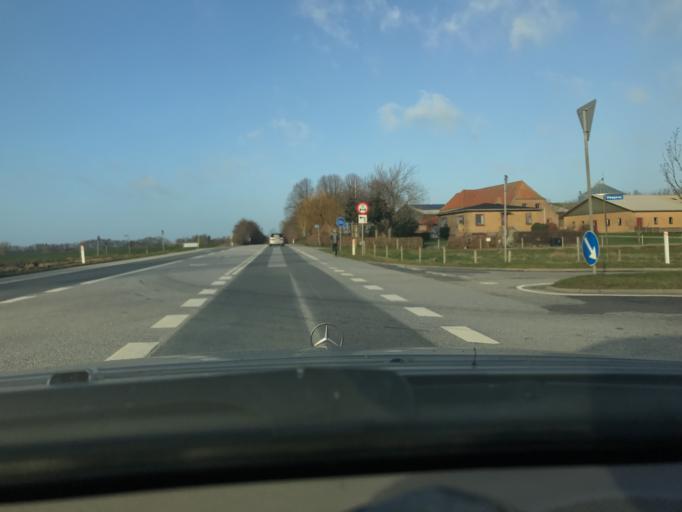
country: DK
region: South Denmark
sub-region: Sonderborg Kommune
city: Horuphav
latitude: 54.8949
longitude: 9.9670
